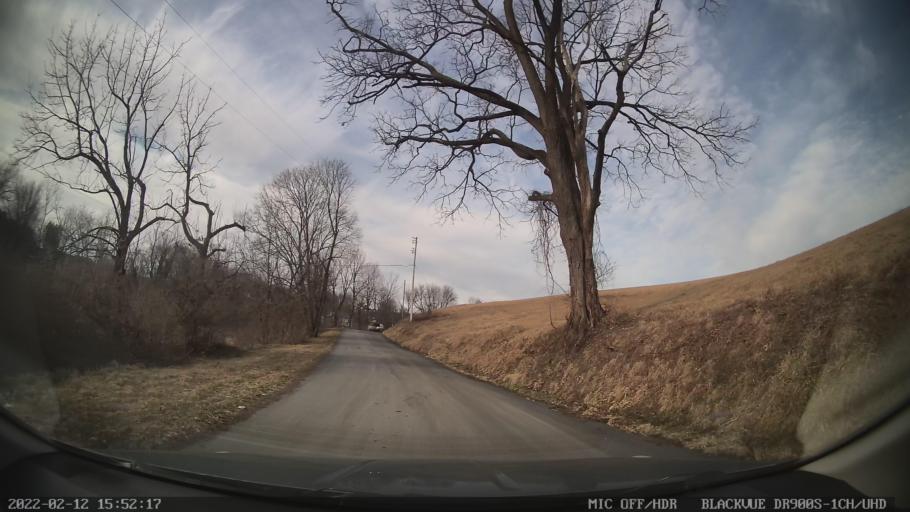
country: US
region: Pennsylvania
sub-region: Berks County
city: Kutztown
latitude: 40.5729
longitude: -75.7683
